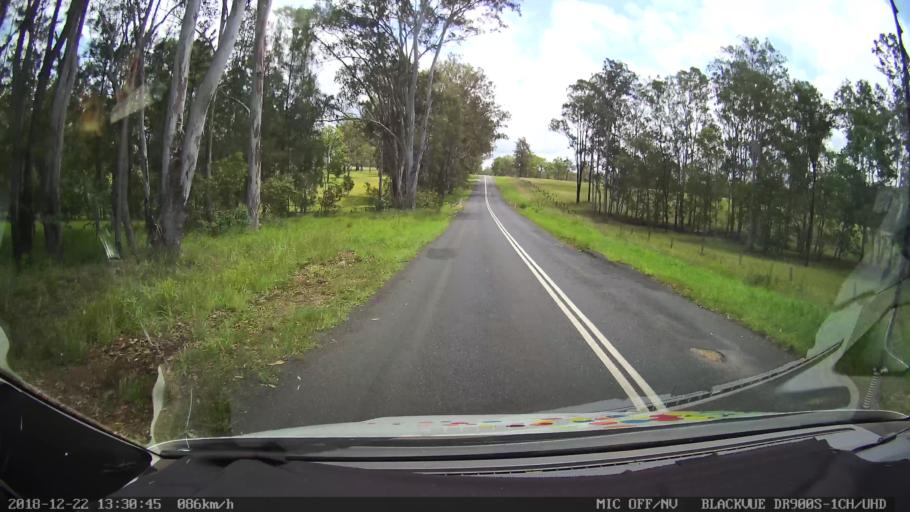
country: AU
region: New South Wales
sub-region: Clarence Valley
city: Coutts Crossing
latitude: -29.8519
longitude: 152.8614
